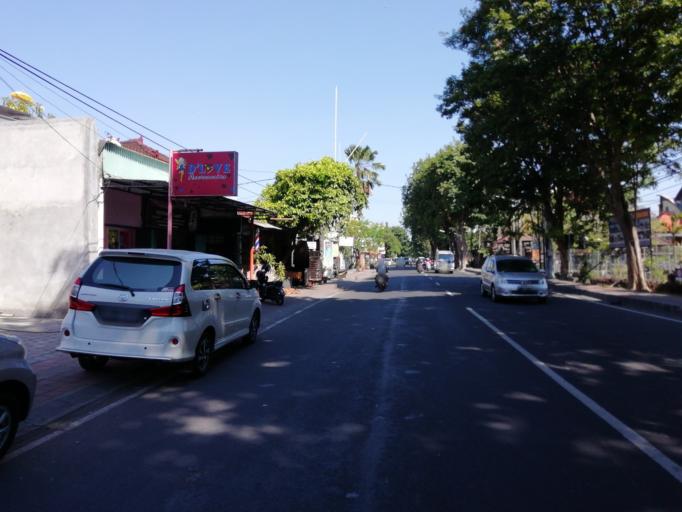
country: ID
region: Bali
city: Karyadharma
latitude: -8.7021
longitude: 115.2196
